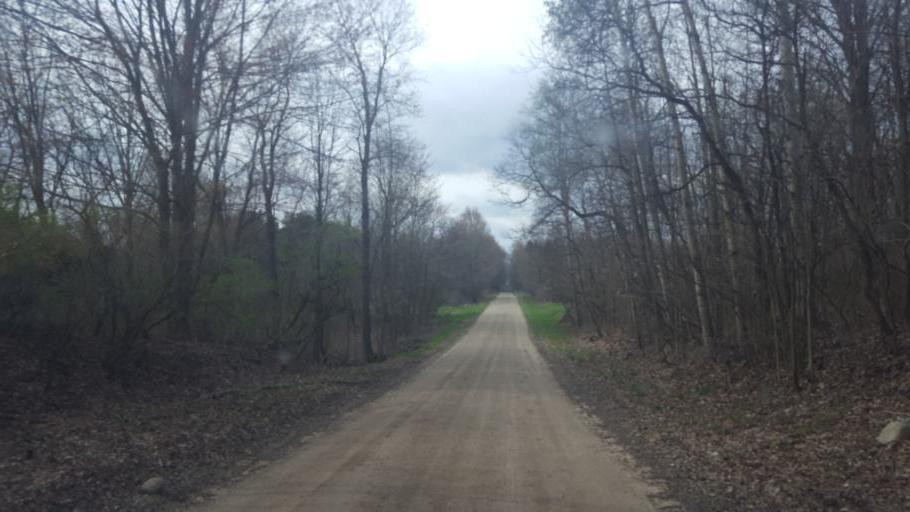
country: US
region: Michigan
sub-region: Isabella County
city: Lake Isabella
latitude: 43.5605
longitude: -85.0064
